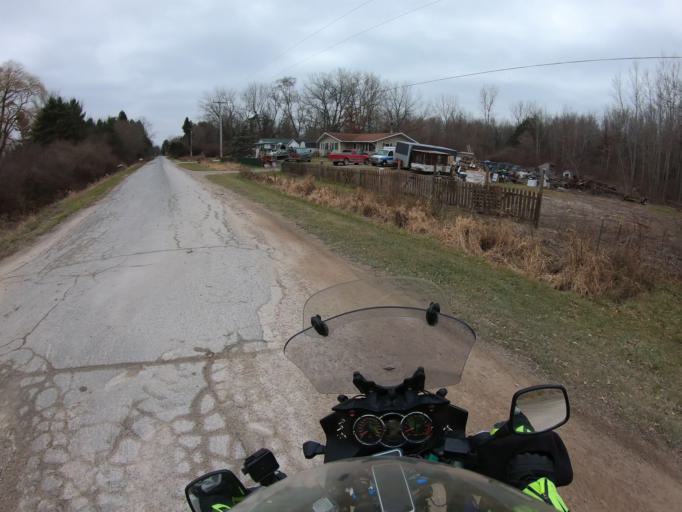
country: US
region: Michigan
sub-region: Saginaw County
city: Saint Charles
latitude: 43.3440
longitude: -84.1316
